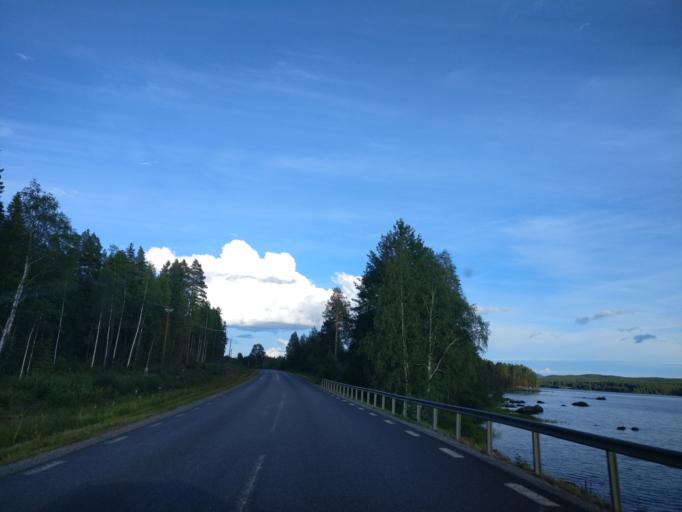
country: SE
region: Jaemtland
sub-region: Braecke Kommun
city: Braecke
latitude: 62.3904
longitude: 15.0457
